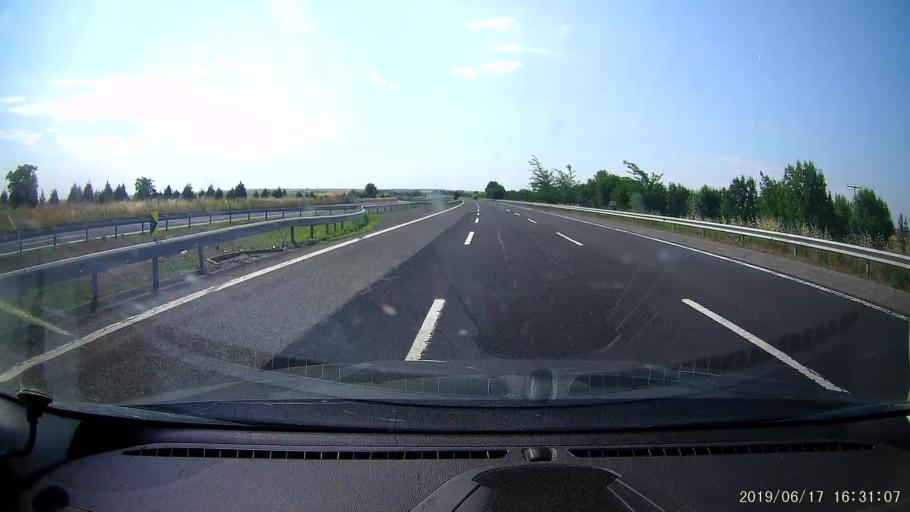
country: TR
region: Tekirdag
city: Beyazkoy
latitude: 41.3582
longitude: 27.6377
